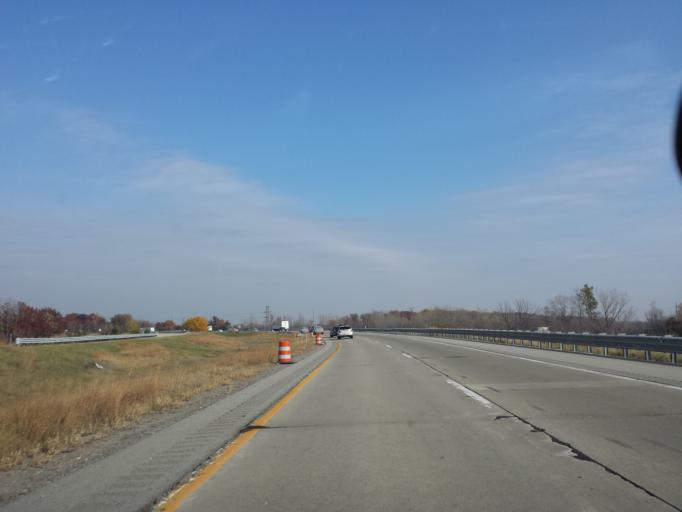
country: US
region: Michigan
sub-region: Saginaw County
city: Zilwaukee
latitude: 43.4966
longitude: -83.9322
